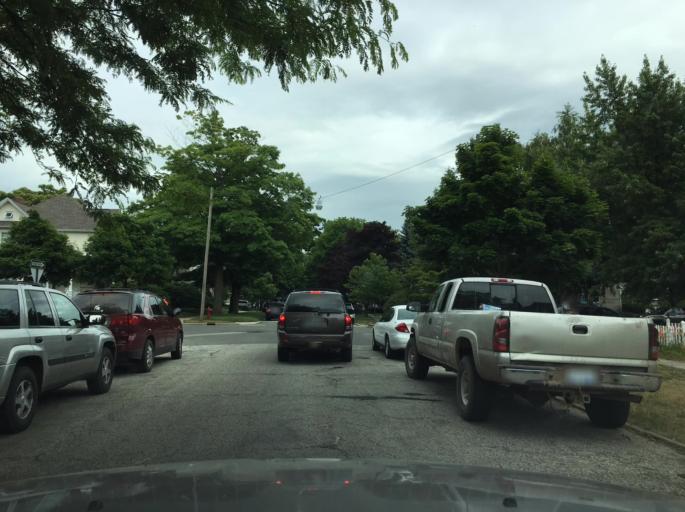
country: US
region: Michigan
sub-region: Mason County
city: Ludington
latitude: 43.9545
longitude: -86.4440
